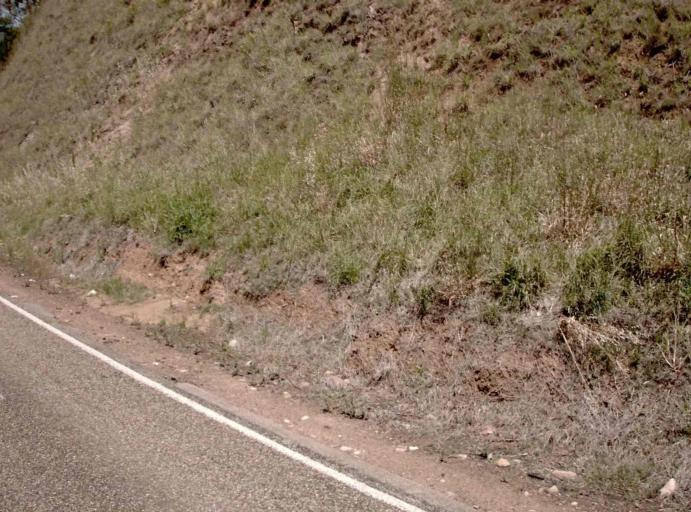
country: AU
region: Victoria
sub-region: East Gippsland
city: Bairnsdale
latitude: -37.3839
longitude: 147.8305
